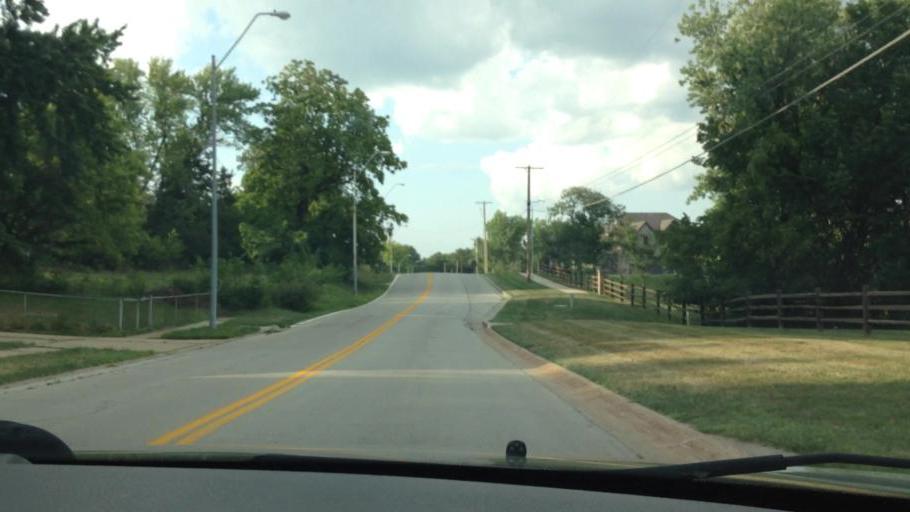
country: US
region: Missouri
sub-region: Platte County
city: Parkville
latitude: 39.2214
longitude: -94.6404
